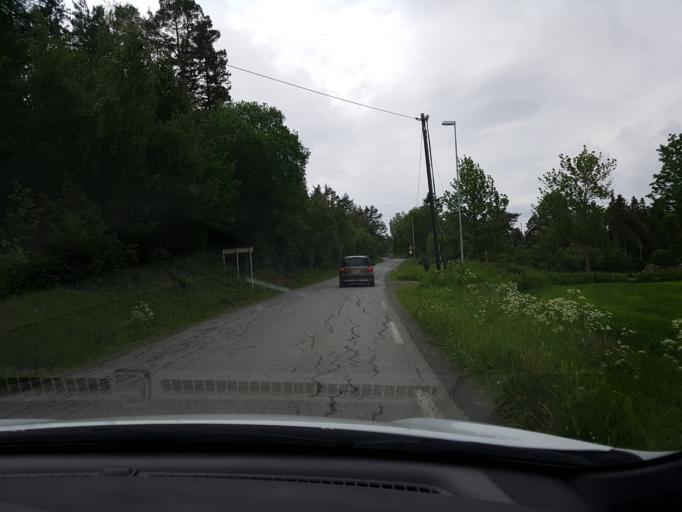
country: NO
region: Nord-Trondelag
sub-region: Frosta
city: Frosta
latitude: 63.6225
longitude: 10.7625
